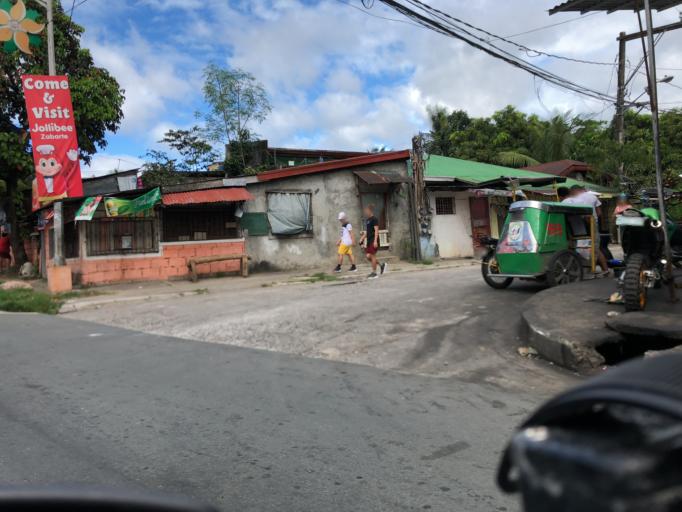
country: PH
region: Central Luzon
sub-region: Province of Bulacan
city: San Jose del Monte
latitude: 14.7446
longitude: 121.0533
